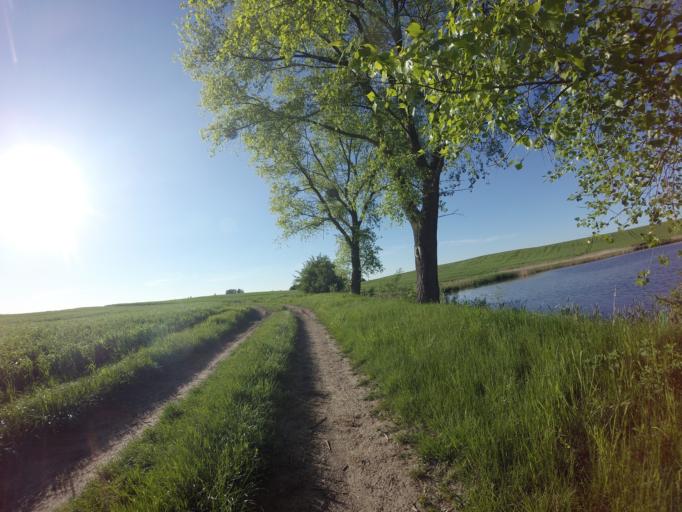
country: PL
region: West Pomeranian Voivodeship
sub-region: Powiat choszczenski
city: Choszczno
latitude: 53.1254
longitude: 15.3614
